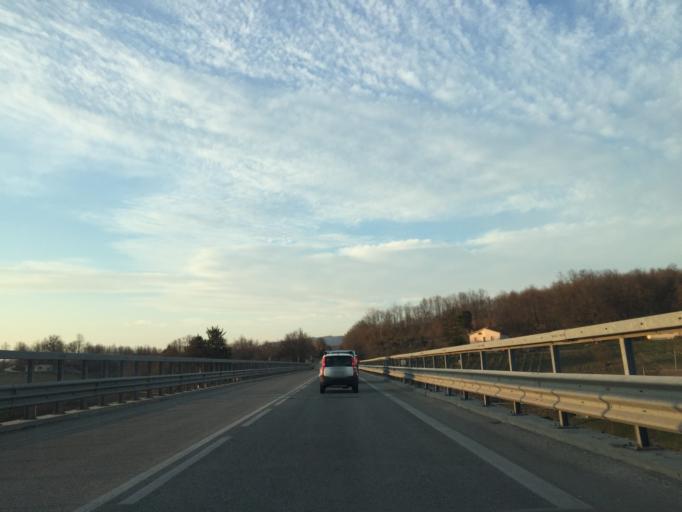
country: IT
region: Molise
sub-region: Provincia di Campobasso
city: Vinchiaturo
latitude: 41.4954
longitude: 14.6098
